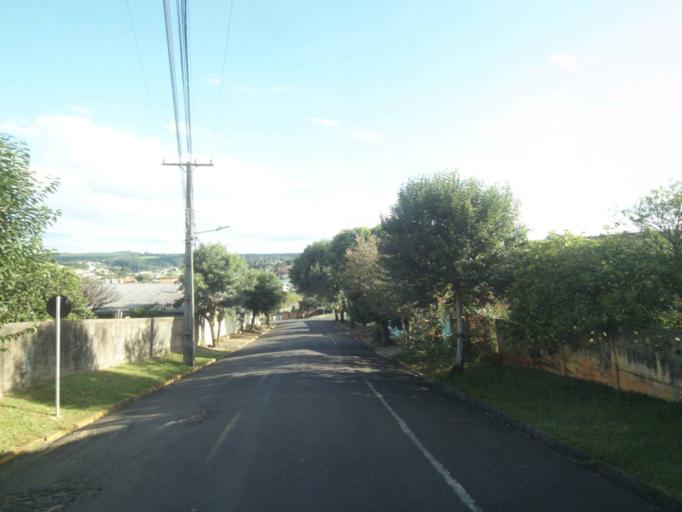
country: BR
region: Parana
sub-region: Telemaco Borba
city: Telemaco Borba
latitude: -24.3334
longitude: -50.6182
